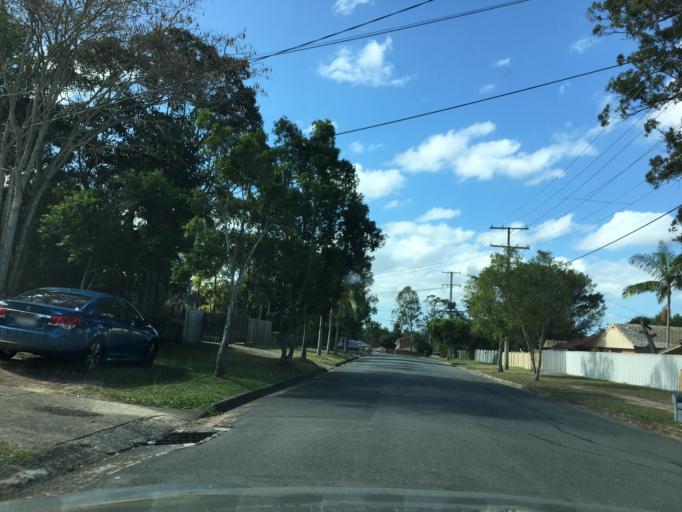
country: AU
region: Queensland
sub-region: Logan
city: Waterford West
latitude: -27.6764
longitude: 153.1271
